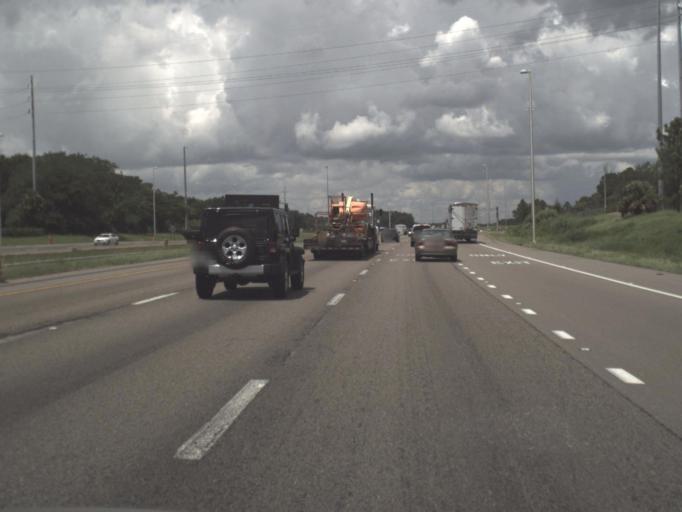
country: US
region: Florida
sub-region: Hillsborough County
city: Temple Terrace
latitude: 28.0423
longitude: -82.3511
